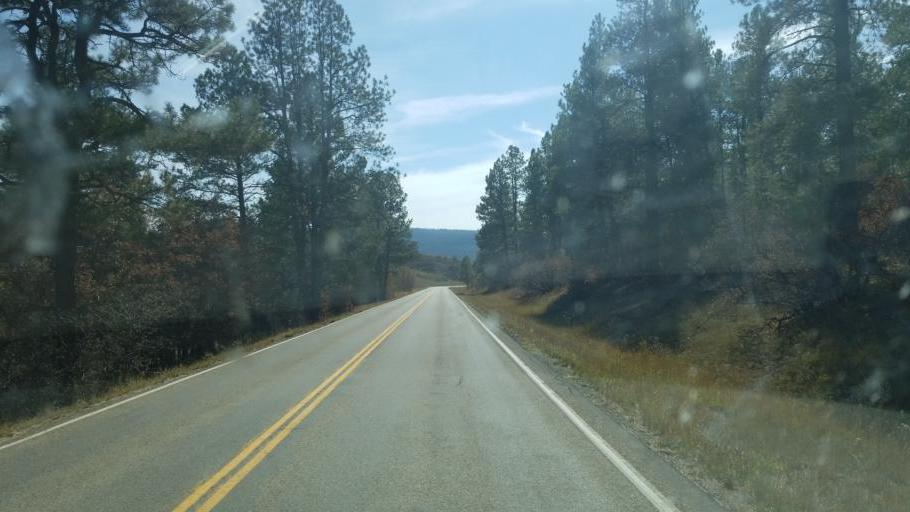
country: US
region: New Mexico
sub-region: Rio Arriba County
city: Dulce
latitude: 37.1006
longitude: -106.9136
